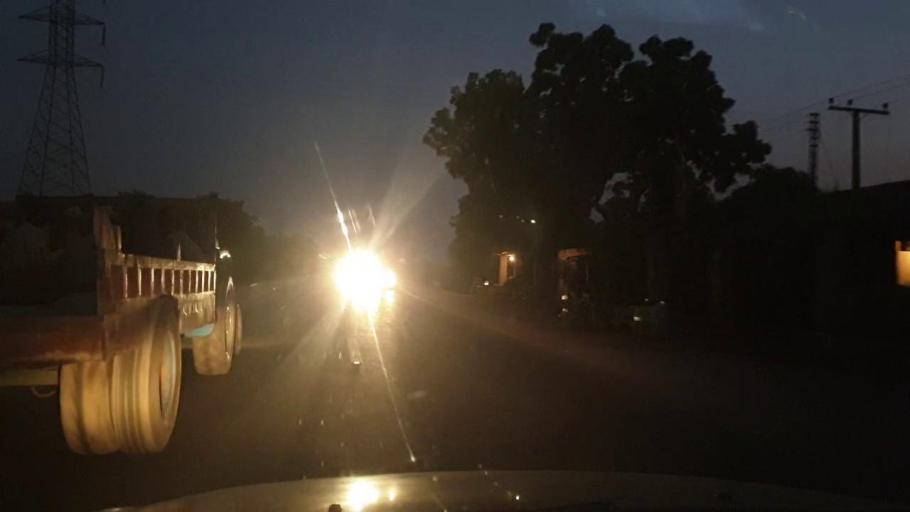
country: PK
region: Sindh
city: Chambar
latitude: 25.3644
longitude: 68.7846
